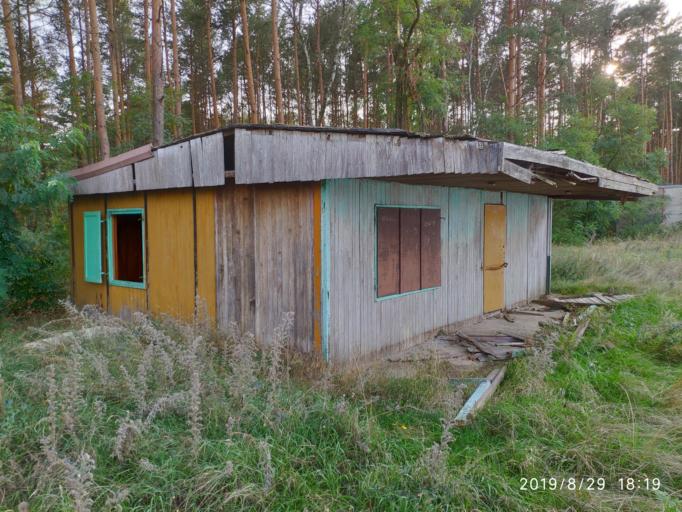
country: PL
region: Lubusz
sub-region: Powiat krosnienski
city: Bobrowice
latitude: 51.9813
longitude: 15.0457
